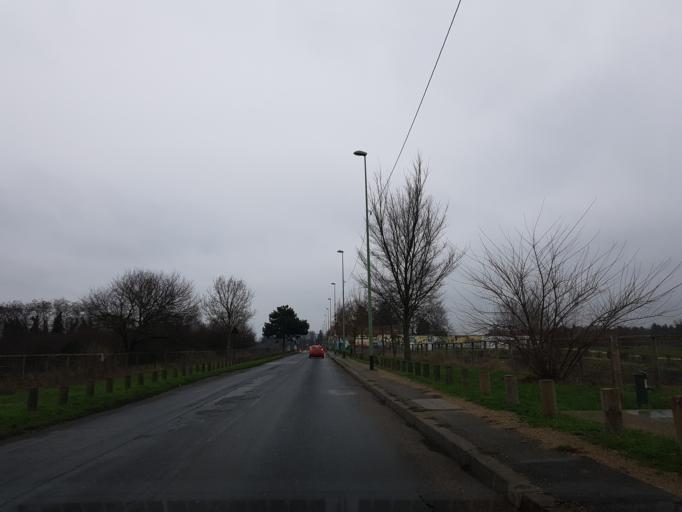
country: FR
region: Ile-de-France
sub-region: Departement du Val-de-Marne
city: Thiais
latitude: 48.7806
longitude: 2.3828
